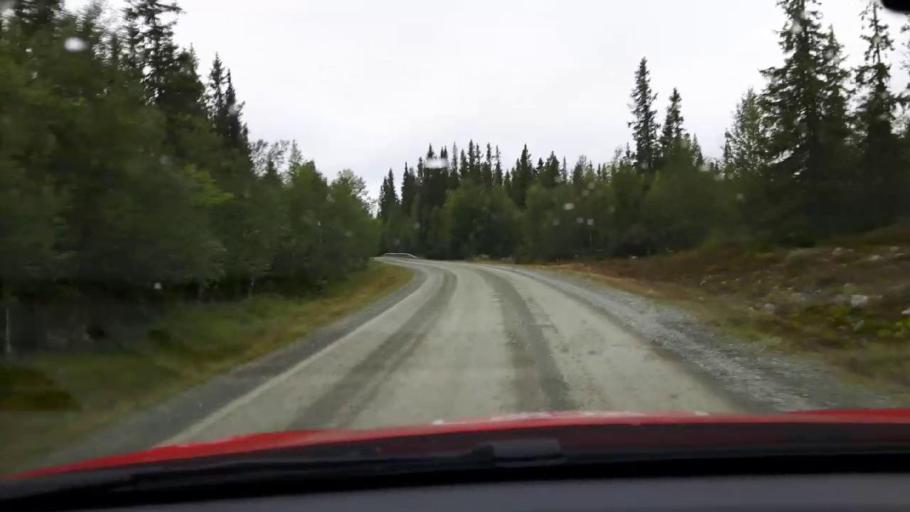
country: SE
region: Jaemtland
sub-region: Bergs Kommun
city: Hoverberg
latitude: 62.8808
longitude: 13.9849
